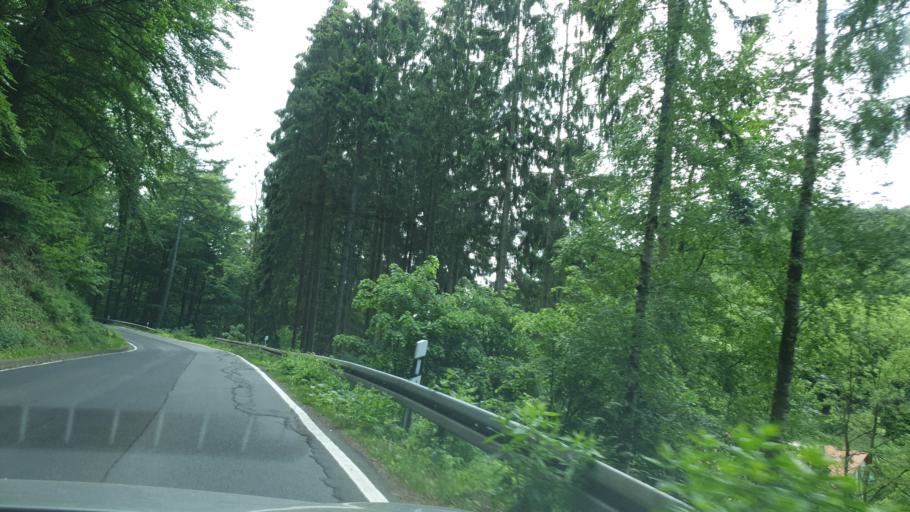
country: DE
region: Rheinland-Pfalz
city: Neuhausel
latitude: 50.3979
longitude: 7.7175
